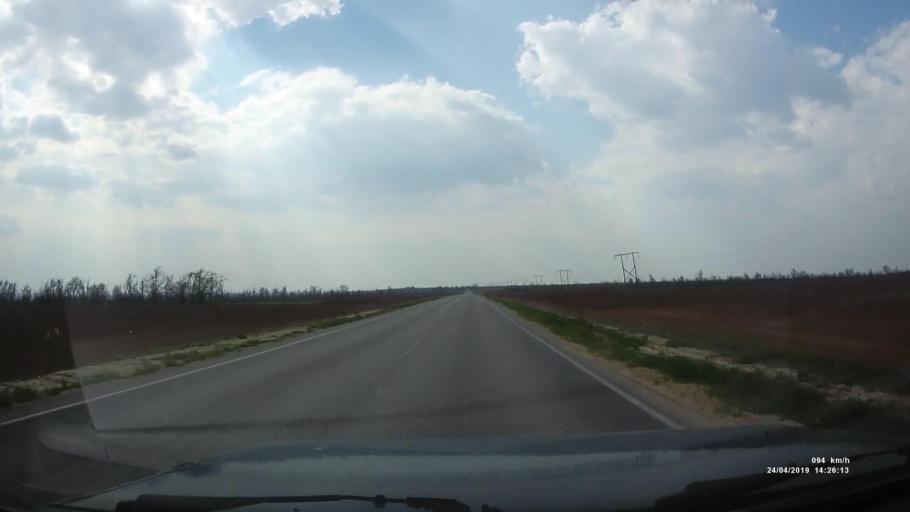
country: RU
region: Kalmykiya
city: Arshan'
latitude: 46.3331
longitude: 44.0669
